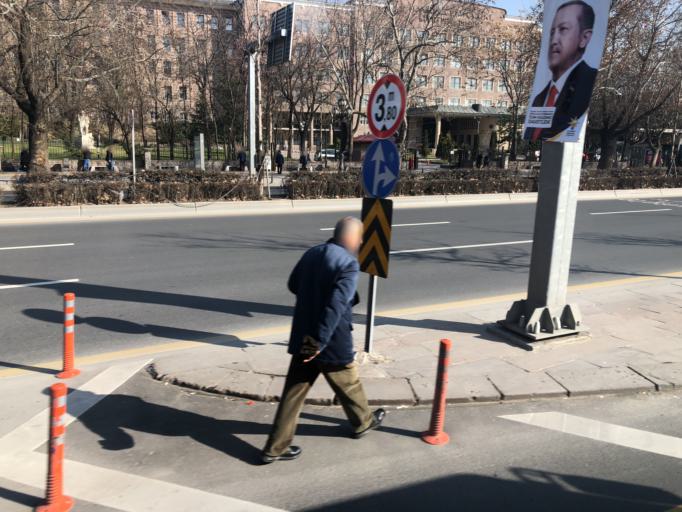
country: TR
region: Ankara
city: Ankara
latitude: 39.9305
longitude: 32.8545
